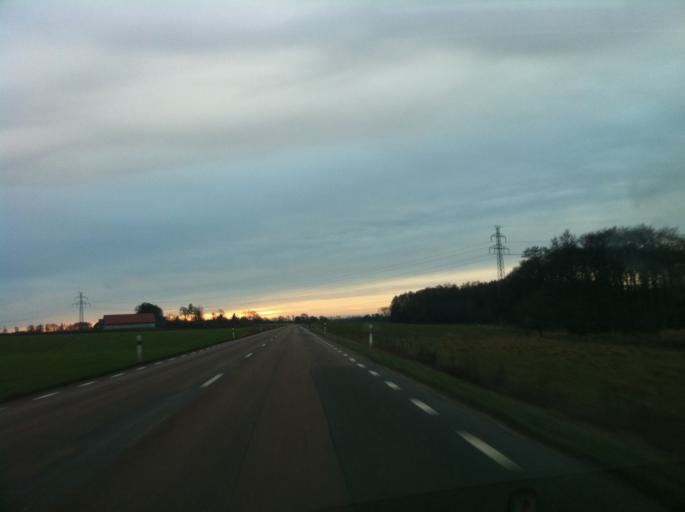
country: SE
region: Skane
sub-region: Bjuvs Kommun
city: Billesholm
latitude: 55.9893
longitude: 12.9411
